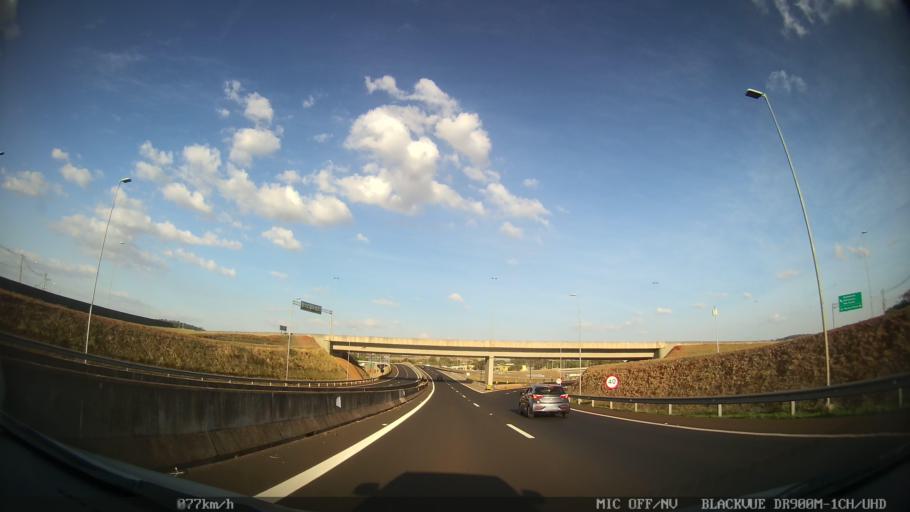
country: BR
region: Sao Paulo
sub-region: Ribeirao Preto
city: Ribeirao Preto
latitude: -21.2047
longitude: -47.7606
